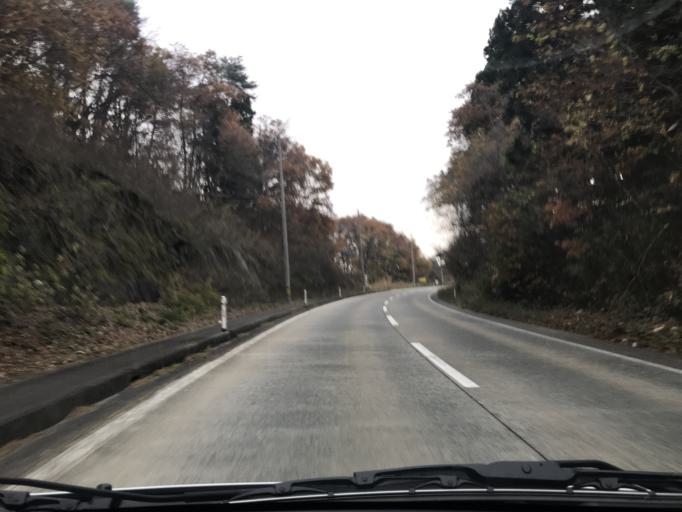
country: JP
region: Iwate
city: Kitakami
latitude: 39.2947
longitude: 141.2115
